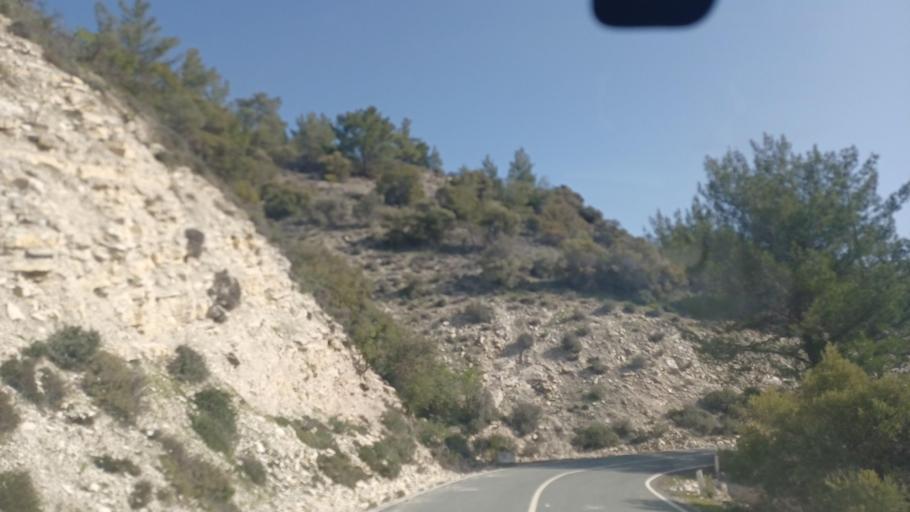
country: CY
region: Limassol
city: Pachna
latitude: 34.8813
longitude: 32.7310
